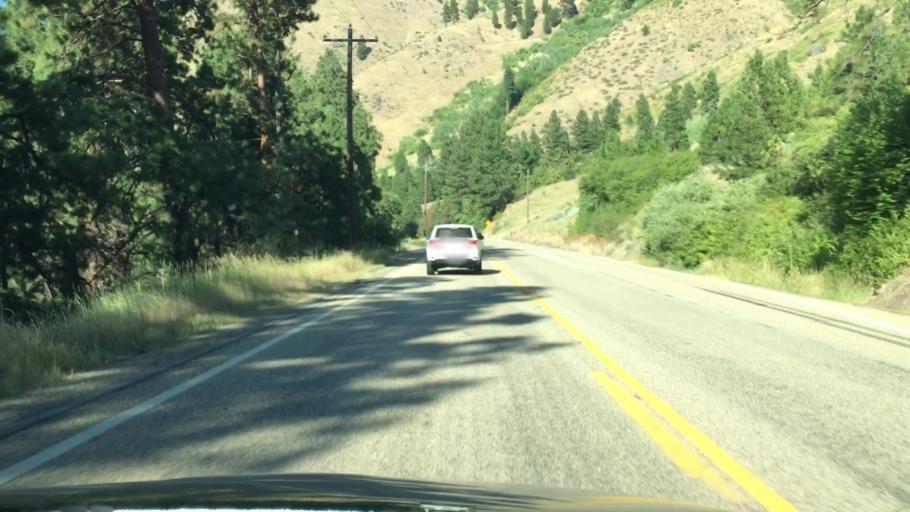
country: US
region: Idaho
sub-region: Boise County
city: Idaho City
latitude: 44.0257
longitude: -116.1397
